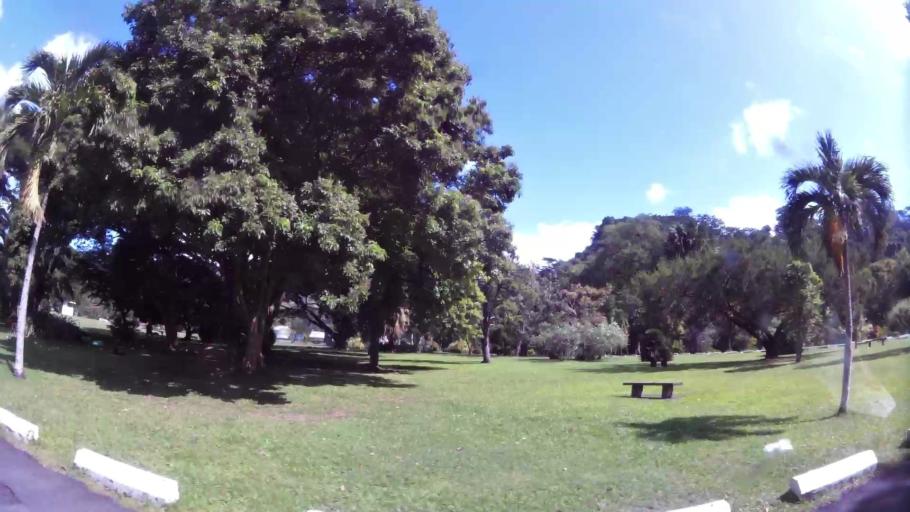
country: DM
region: Saint George
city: Roseau
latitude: 15.3001
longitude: -61.3826
